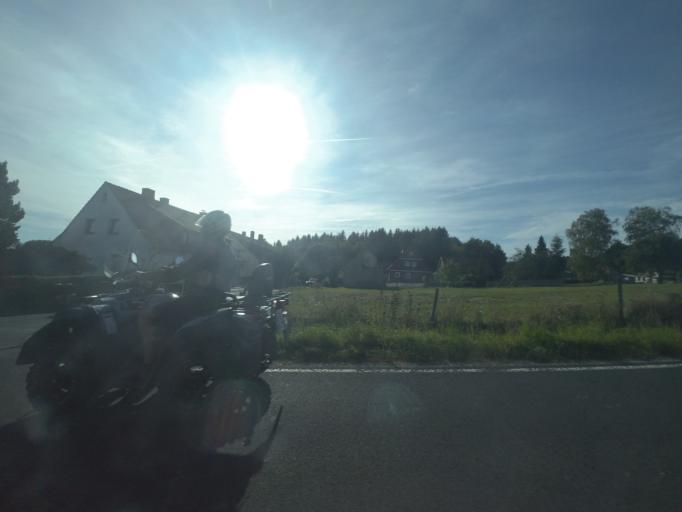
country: DE
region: Hesse
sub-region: Regierungsbezirk Kassel
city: Poppenhausen
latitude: 50.5156
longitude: 9.8701
